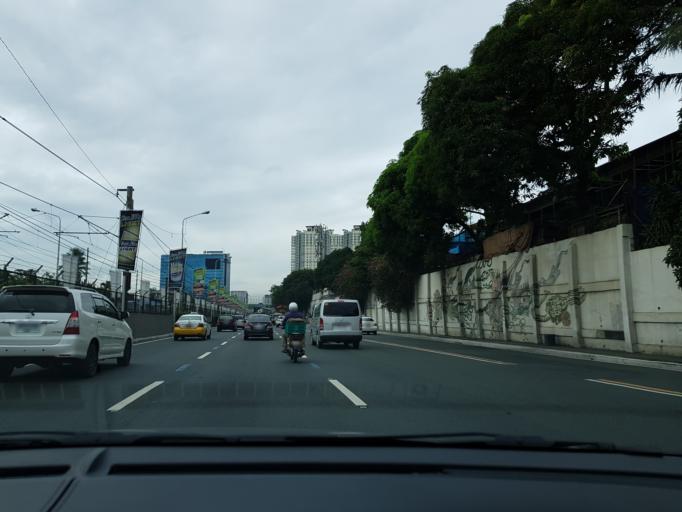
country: PH
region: Metro Manila
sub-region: Makati City
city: Makati City
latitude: 14.5453
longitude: 121.0233
